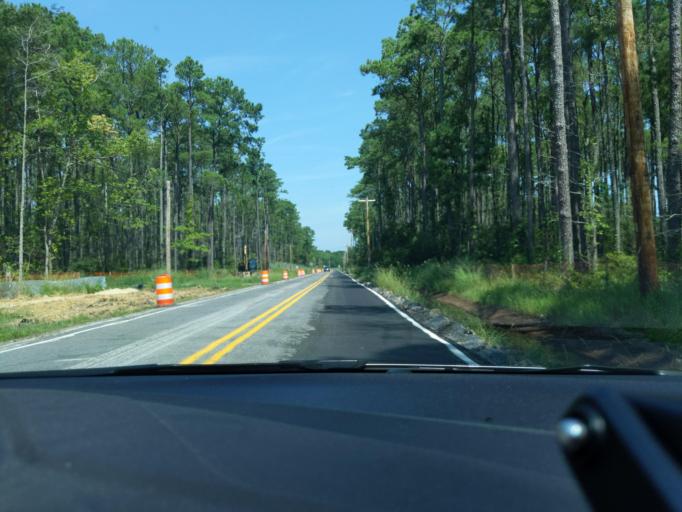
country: US
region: Virginia
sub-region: Northumberland County
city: Heathsville
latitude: 38.0654
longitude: -76.3361
